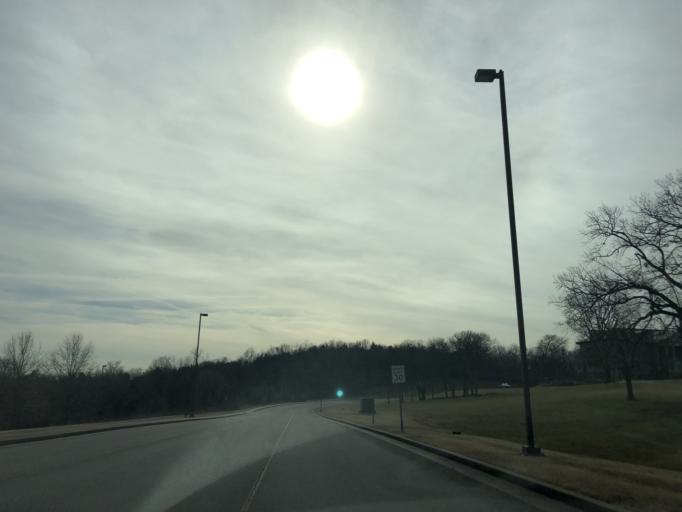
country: US
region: Tennessee
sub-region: Davidson County
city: Nashville
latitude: 36.2145
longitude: -86.7398
